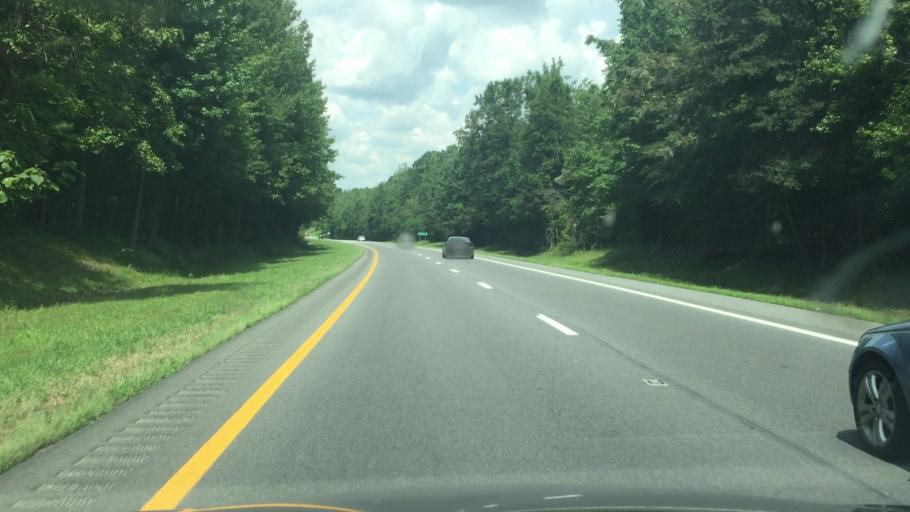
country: US
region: North Carolina
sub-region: Guilford County
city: Pleasant Garden
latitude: 35.9094
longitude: -79.8215
